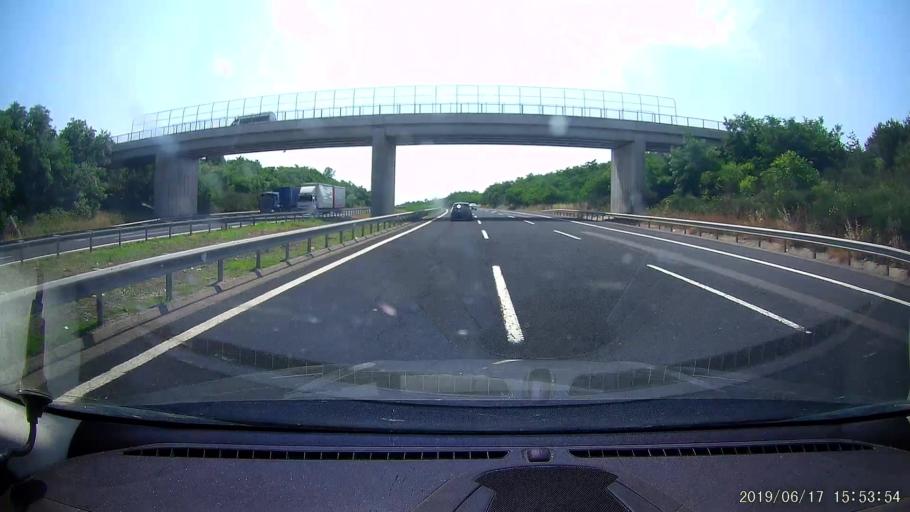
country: TR
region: Istanbul
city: Buyukcavuslu
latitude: 41.2020
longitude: 28.0607
